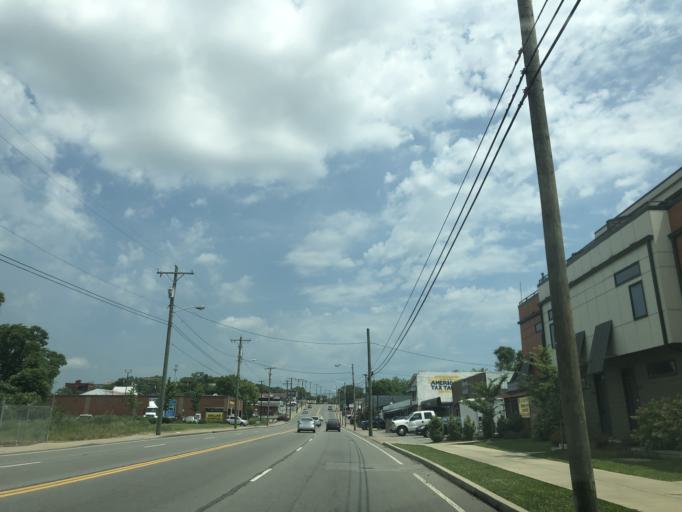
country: US
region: Tennessee
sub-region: Davidson County
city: Nashville
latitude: 36.1903
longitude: -86.7728
